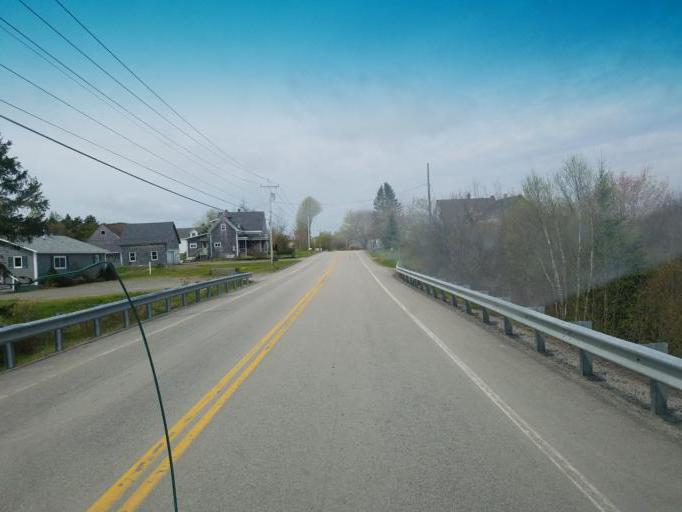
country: US
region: Maine
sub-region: Washington County
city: Eastport
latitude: 44.7899
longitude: -67.1677
